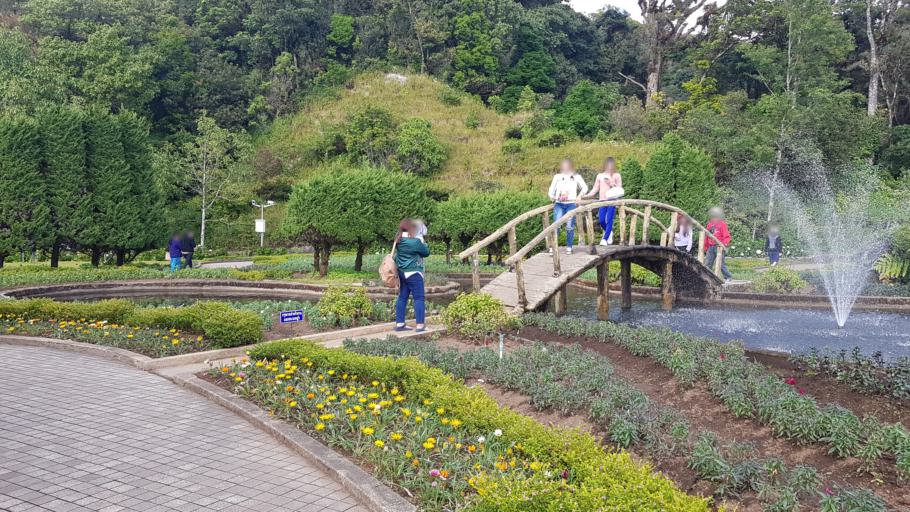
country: TH
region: Chiang Mai
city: Mae Chaem
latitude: 18.5535
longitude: 98.4791
